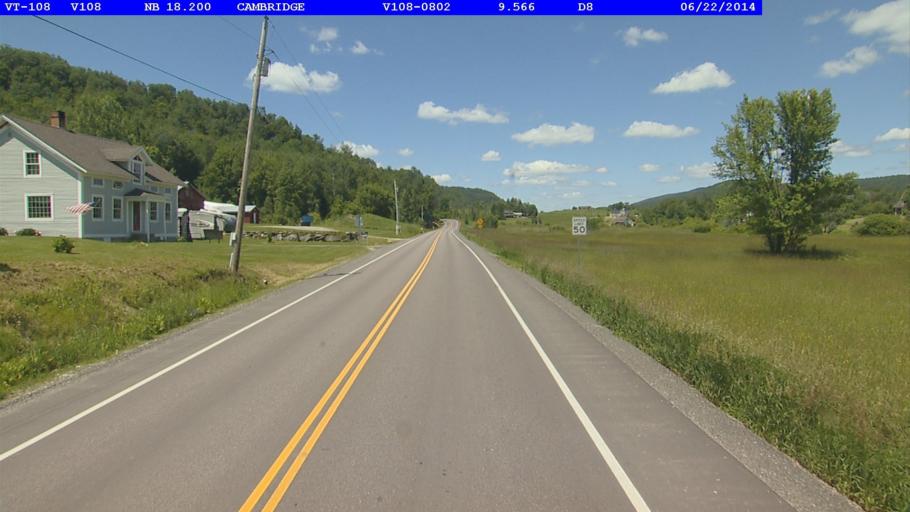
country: US
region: Vermont
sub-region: Lamoille County
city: Johnson
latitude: 44.6540
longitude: -72.8280
